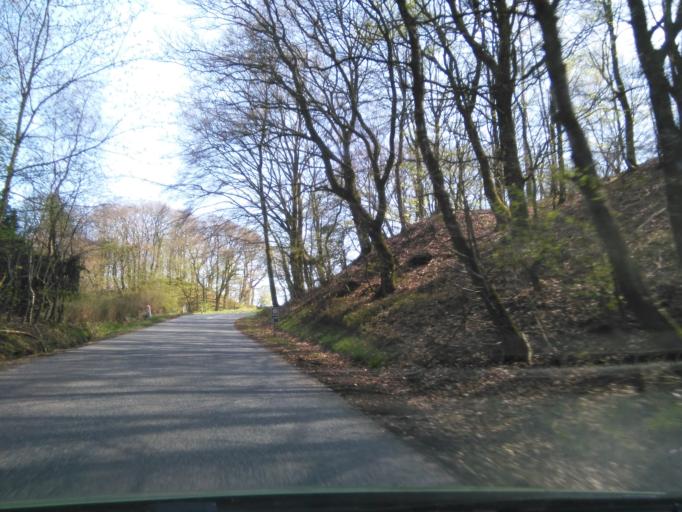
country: DK
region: Central Jutland
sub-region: Viborg Kommune
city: Viborg
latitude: 56.3608
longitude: 9.3392
